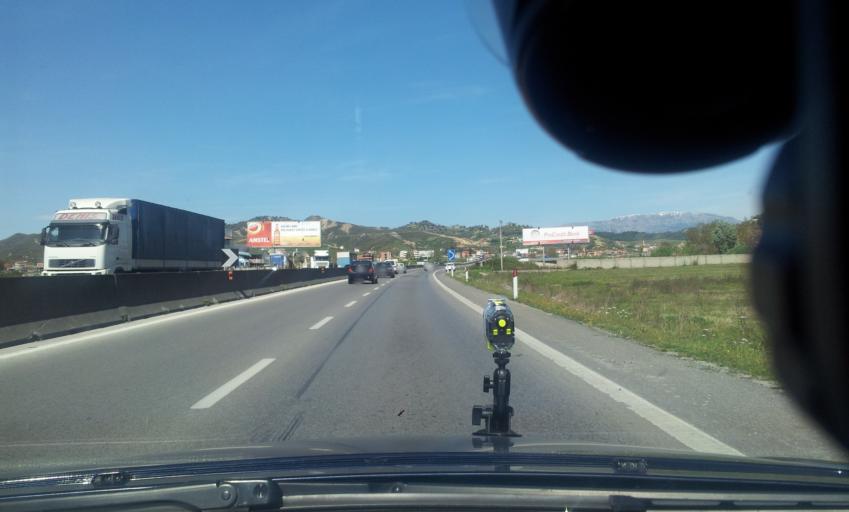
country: AL
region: Tirane
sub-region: Rrethi i Tiranes
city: Vore
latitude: 41.3920
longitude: 19.6320
